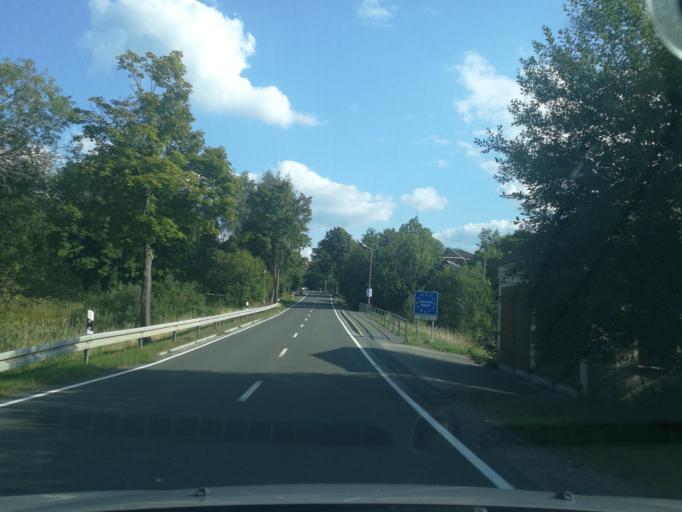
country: DE
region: Saxony
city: Eichigt
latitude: 50.3255
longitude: 12.1567
